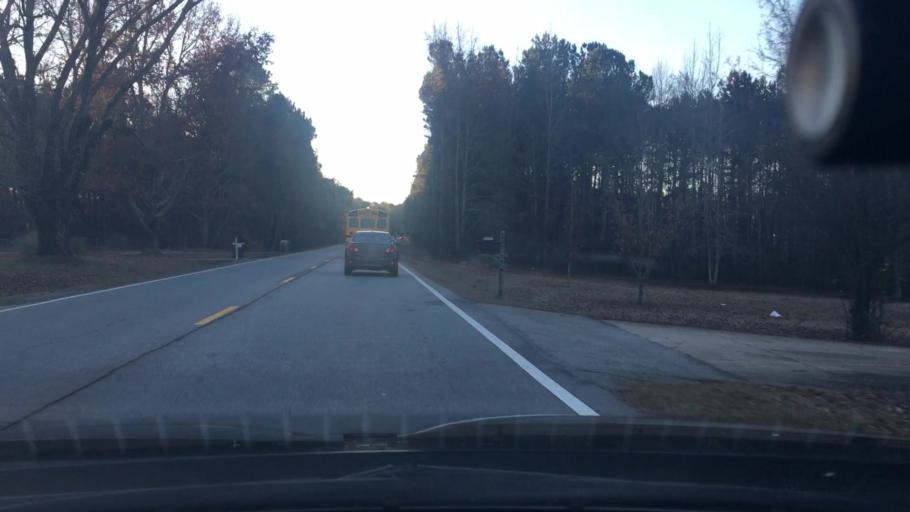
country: US
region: Georgia
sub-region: Fayette County
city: Peachtree City
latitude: 33.3551
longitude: -84.6595
